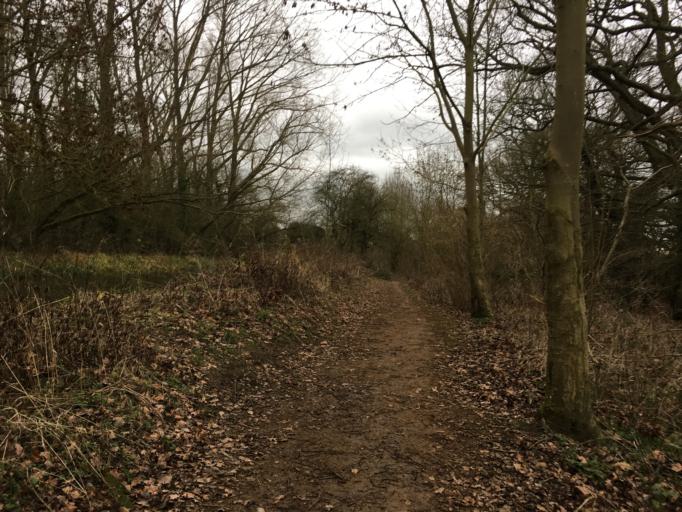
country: GB
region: England
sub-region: Warwickshire
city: Rugby
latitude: 52.3989
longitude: -1.2597
